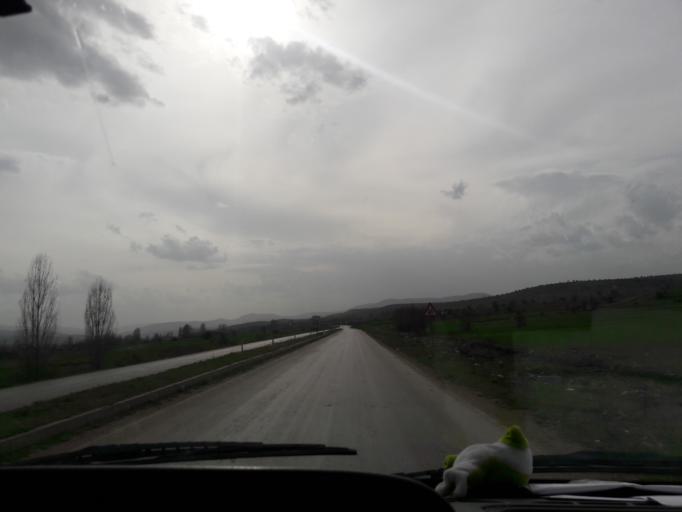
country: TR
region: Gumushane
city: Siran
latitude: 40.1773
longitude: 39.1027
